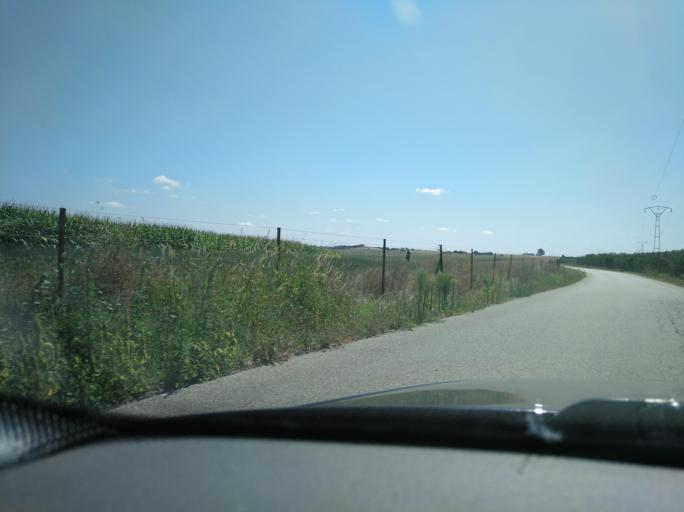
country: ES
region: Extremadura
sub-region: Provincia de Badajoz
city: Olivenza
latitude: 38.7309
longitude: -7.2252
